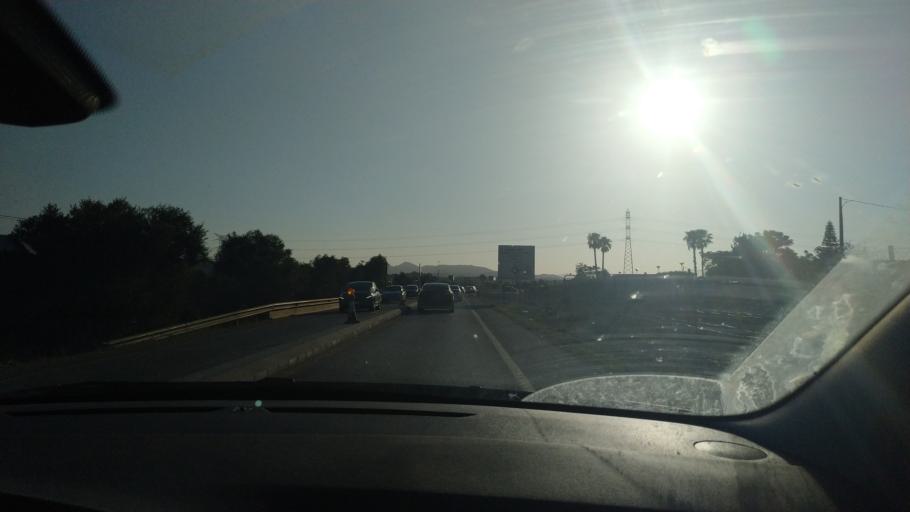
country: ES
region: Valencia
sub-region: Provincia de Alicante
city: Javea
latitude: 38.7754
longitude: 0.1329
